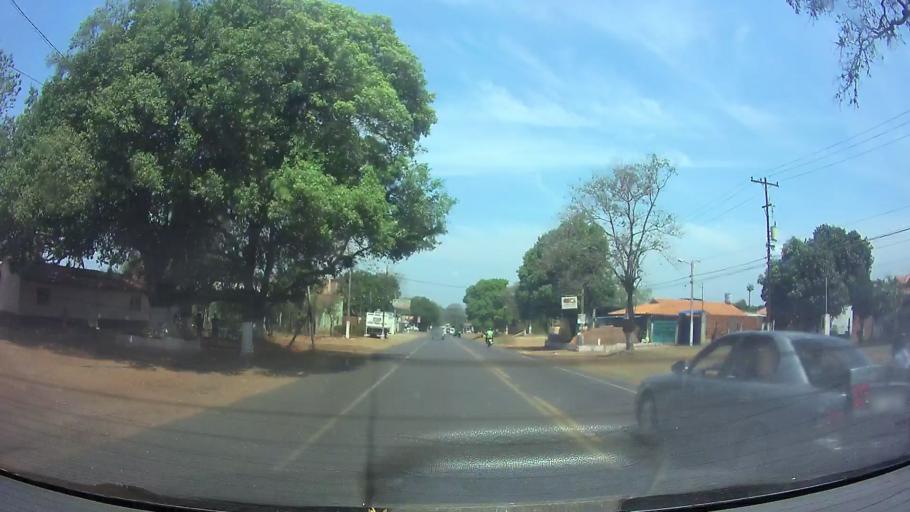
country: PY
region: Central
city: Capiata
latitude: -25.4097
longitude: -57.4600
